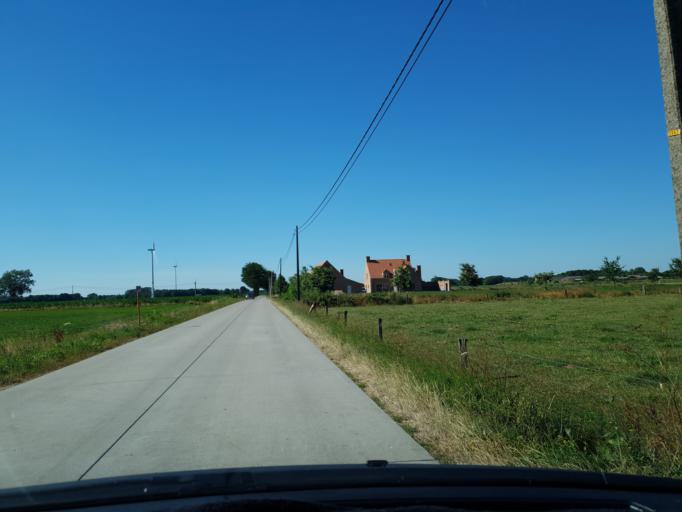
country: BE
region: Flanders
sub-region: Provincie Antwerpen
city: Hoogstraten
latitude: 51.4180
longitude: 4.7244
